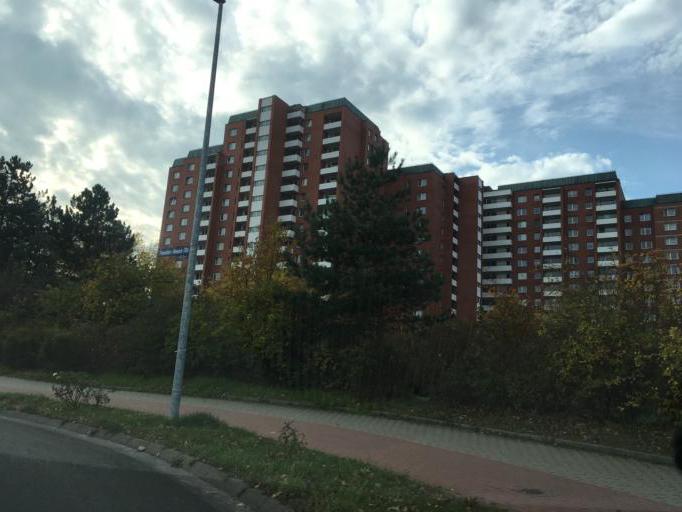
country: DE
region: Lower Saxony
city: Lueneburg
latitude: 53.2388
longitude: 10.4336
